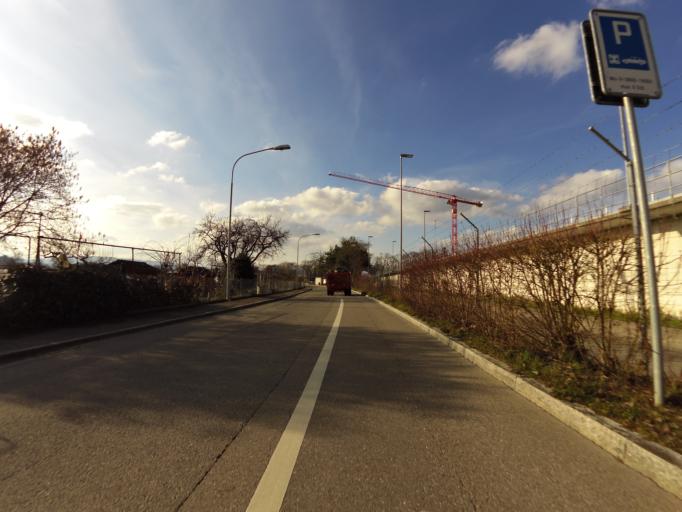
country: CH
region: Zurich
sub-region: Bezirk Zuerich
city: Zuerich (Kreis 10) / Ruetihof
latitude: 47.4015
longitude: 8.4771
